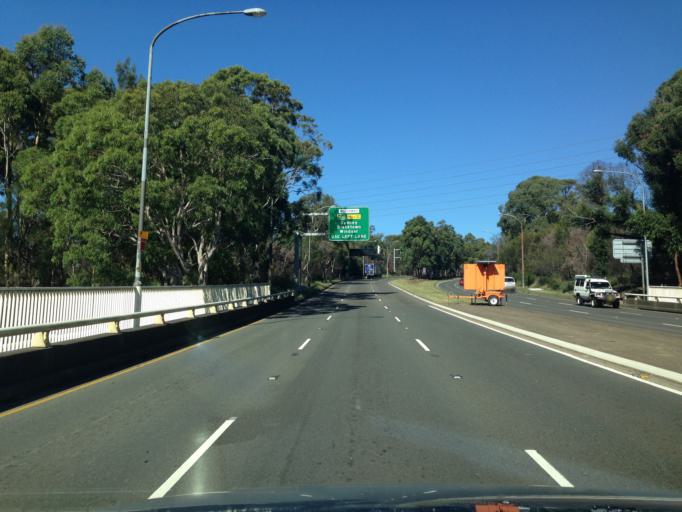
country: AU
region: New South Wales
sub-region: Ryde
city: Macquarie Park
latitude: -33.7760
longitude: 151.1355
